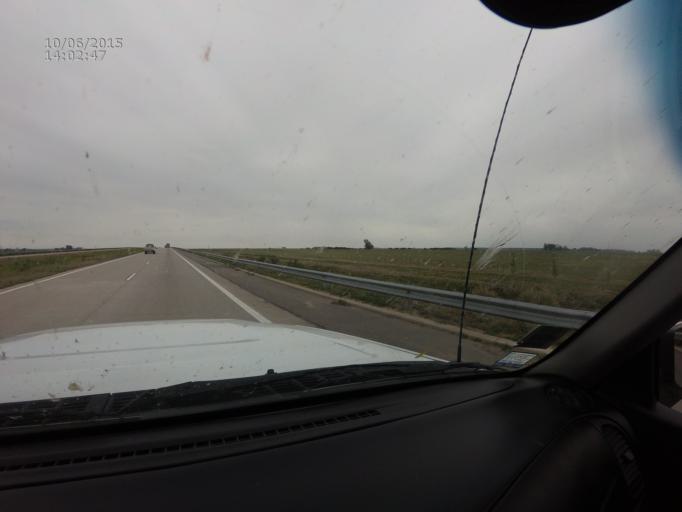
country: AR
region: Cordoba
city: Morrison
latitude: -32.5264
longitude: -62.9380
